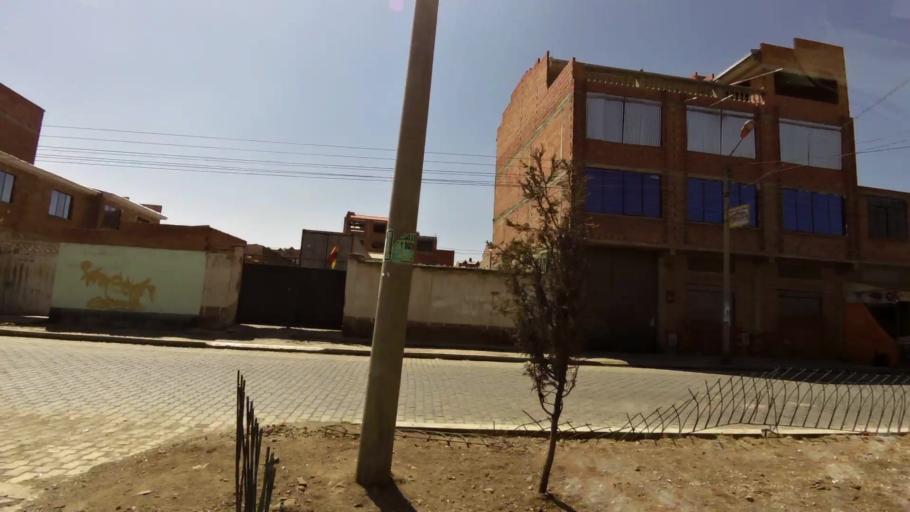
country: BO
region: La Paz
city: La Paz
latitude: -16.5346
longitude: -68.1618
